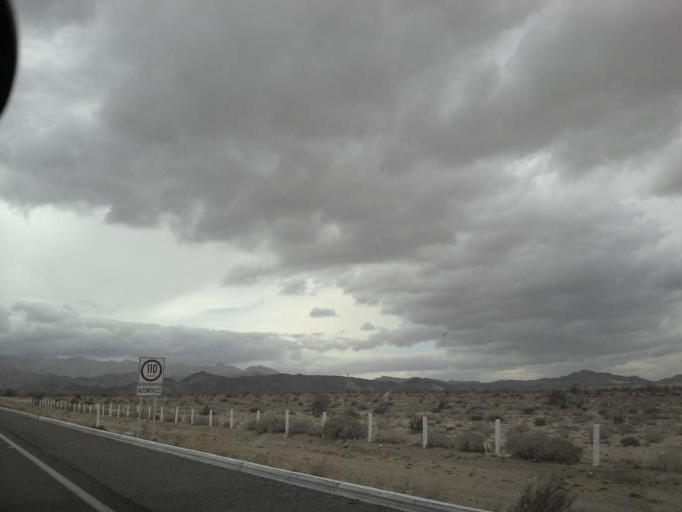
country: US
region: California
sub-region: Imperial County
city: Seeley
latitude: 32.5657
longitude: -115.9020
